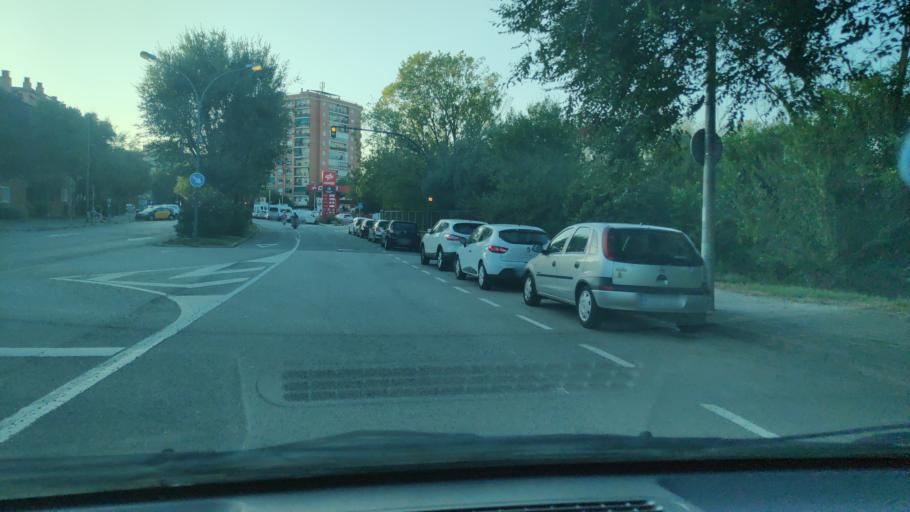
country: ES
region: Catalonia
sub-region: Provincia de Barcelona
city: Ripollet
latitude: 41.4884
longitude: 2.1526
